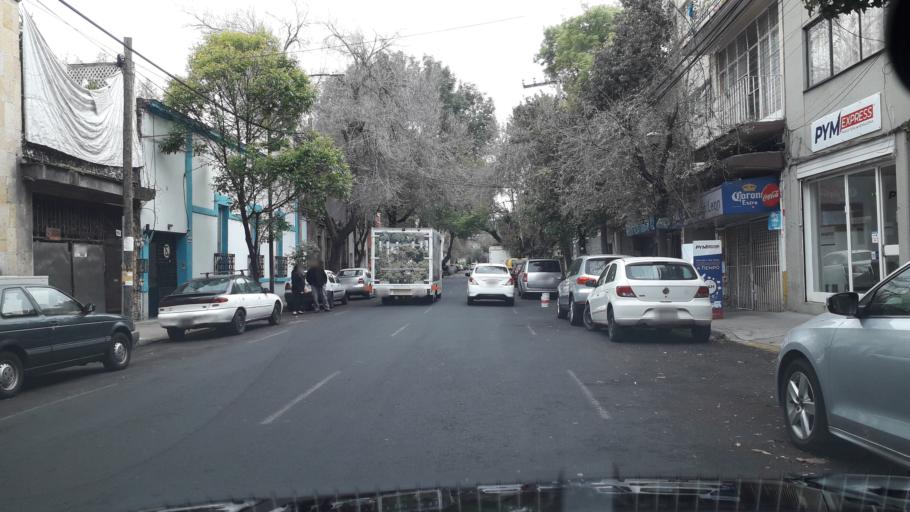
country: MX
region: Mexico City
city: Cuauhtemoc
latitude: 19.4456
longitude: -99.1596
